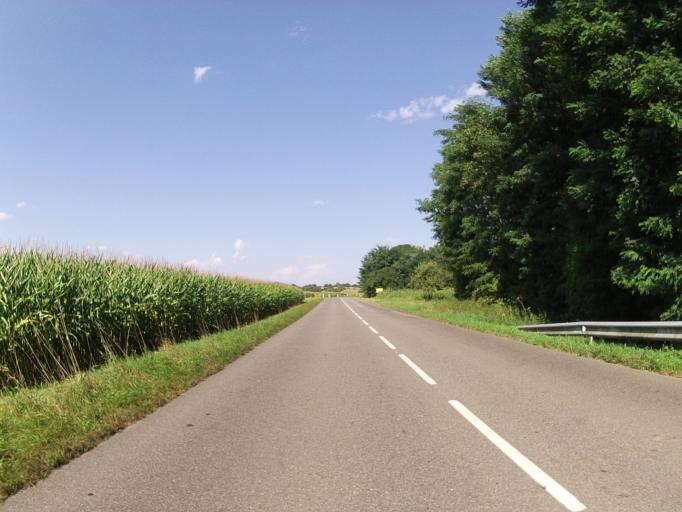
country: FR
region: Alsace
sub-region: Departement du Bas-Rhin
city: Seltz
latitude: 48.9196
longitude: 8.1305
